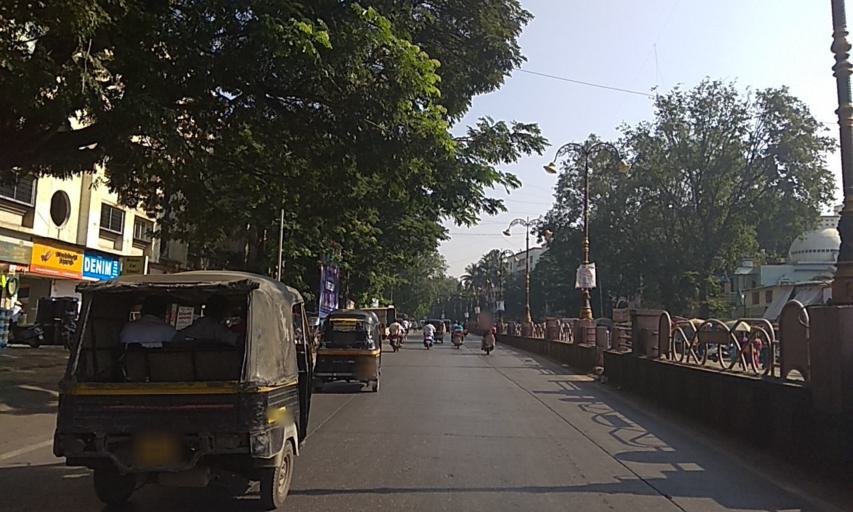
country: IN
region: Maharashtra
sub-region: Pune Division
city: Pune
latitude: 18.4991
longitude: 73.8425
